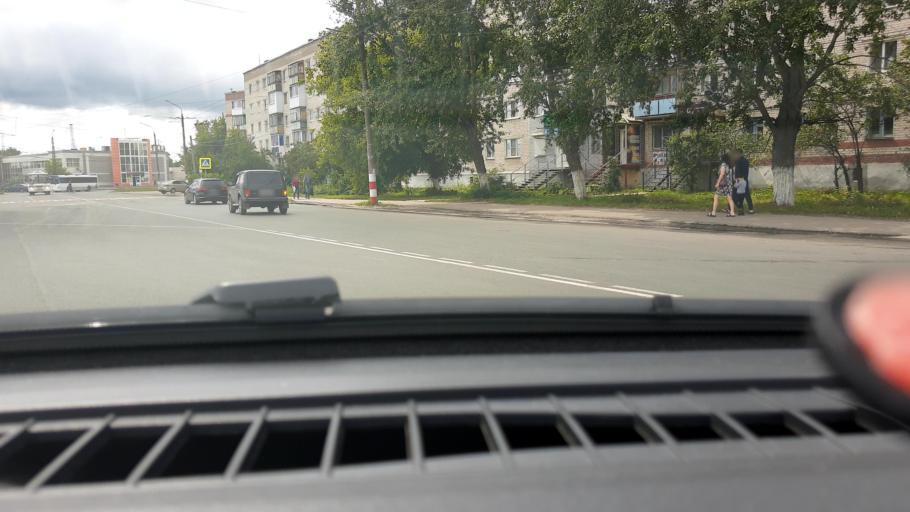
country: RU
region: Nizjnij Novgorod
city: Dzerzhinsk
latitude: 56.2313
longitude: 43.4572
